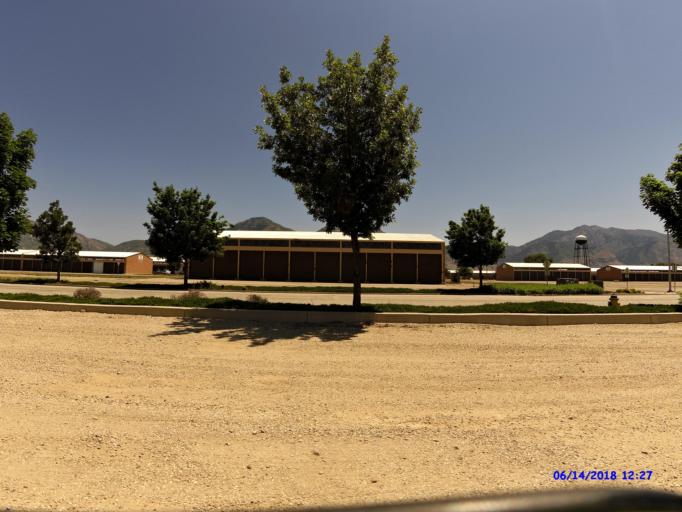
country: US
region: Utah
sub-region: Weber County
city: Harrisville
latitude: 41.2616
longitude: -111.9985
